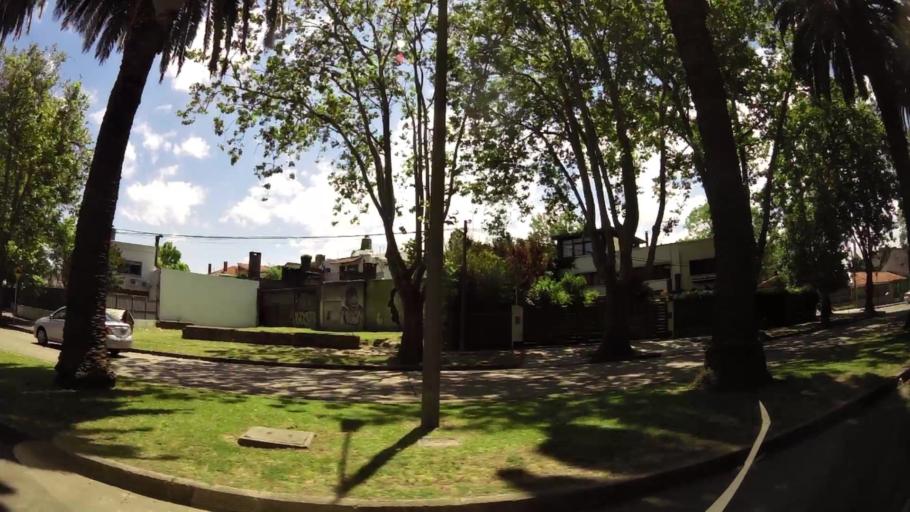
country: UY
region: Montevideo
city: Montevideo
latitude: -34.8676
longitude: -56.1999
